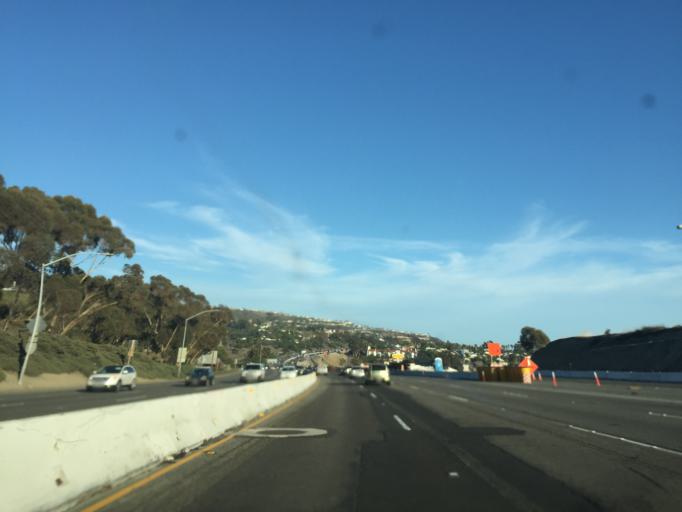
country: US
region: California
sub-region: Orange County
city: San Clemente
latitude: 33.4416
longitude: -117.6269
